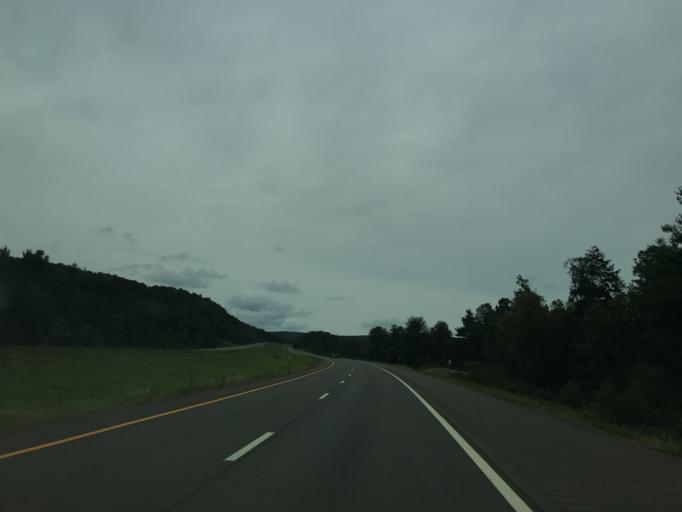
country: US
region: New York
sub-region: Broome County
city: Chenango Bridge
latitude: 42.1675
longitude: -75.7602
